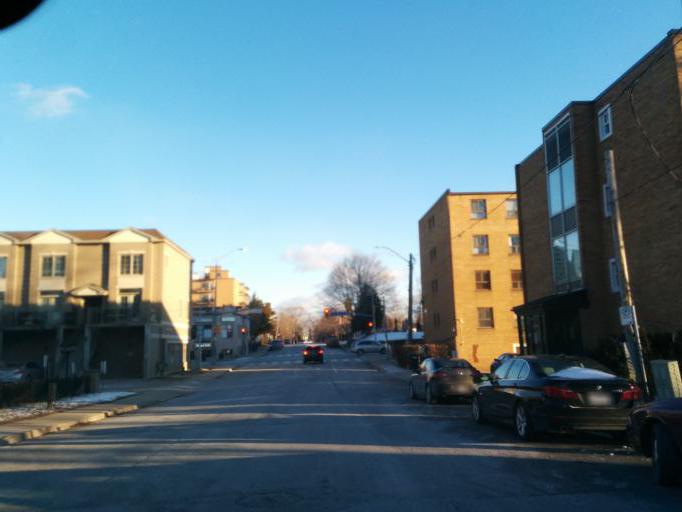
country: CA
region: Ontario
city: Mississauga
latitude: 43.5499
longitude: -79.5888
